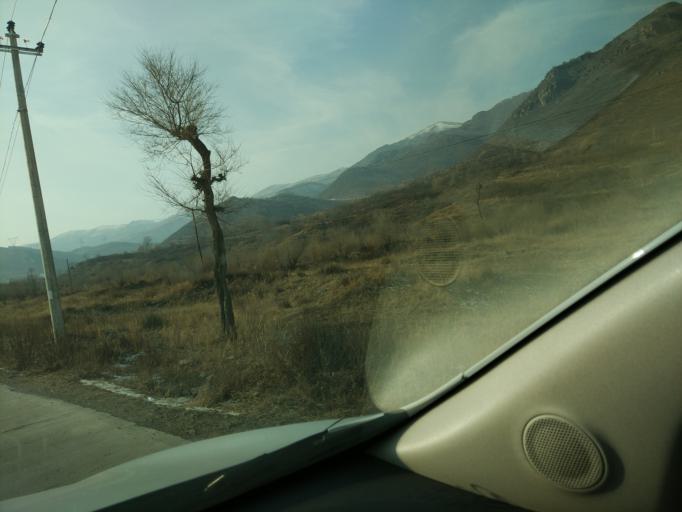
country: CN
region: Hebei
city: Xiwanzi
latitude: 40.8162
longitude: 115.4714
